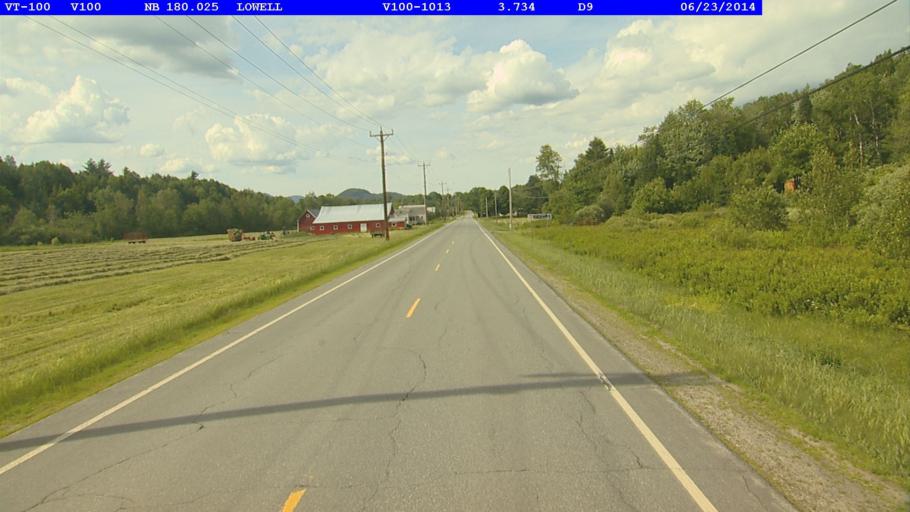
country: US
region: Vermont
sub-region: Lamoille County
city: Hyde Park
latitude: 44.7899
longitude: -72.4485
